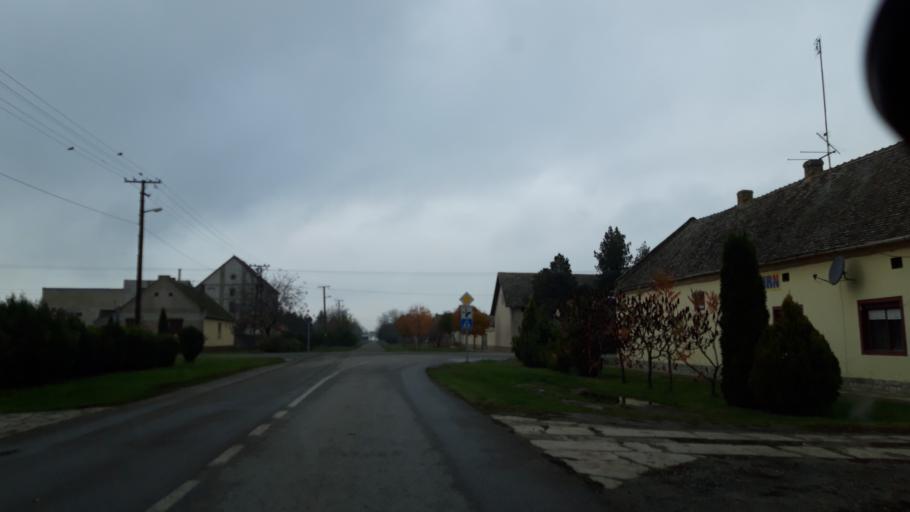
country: RS
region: Autonomna Pokrajina Vojvodina
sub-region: Juznobacki Okrug
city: Temerin
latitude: 45.5067
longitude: 19.9228
